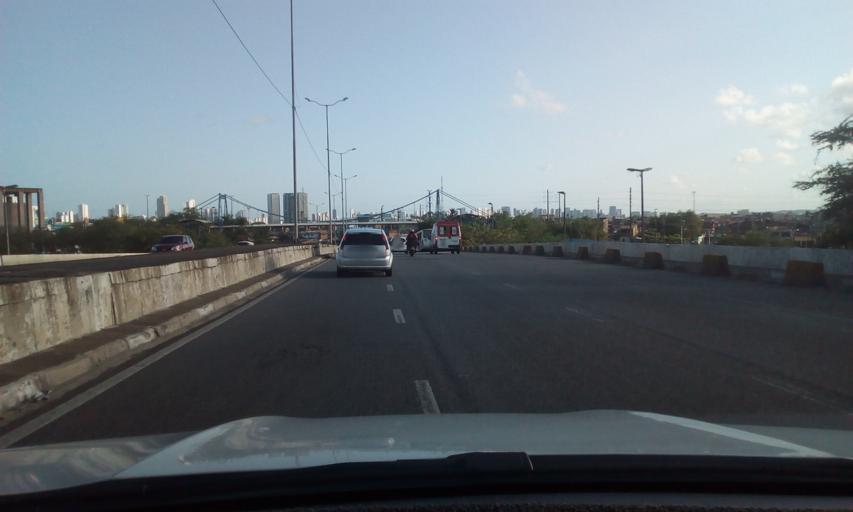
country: BR
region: Pernambuco
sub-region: Recife
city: Recife
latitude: -8.0681
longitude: -34.8968
